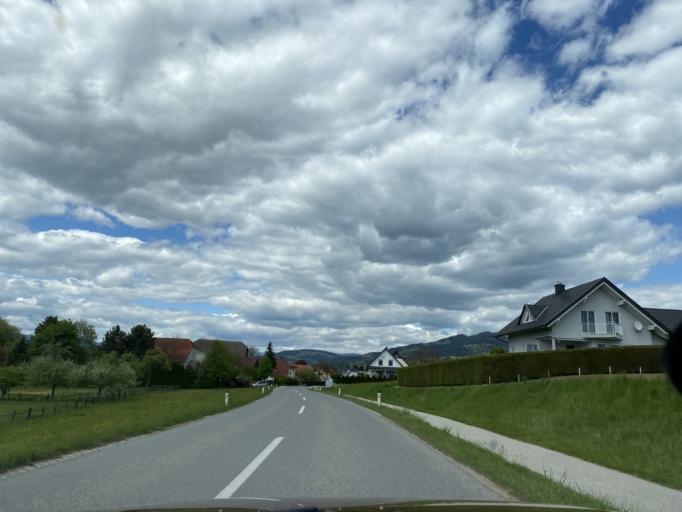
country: AT
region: Carinthia
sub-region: Politischer Bezirk Wolfsberg
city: Sankt Andrae
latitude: 46.7967
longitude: 14.8507
